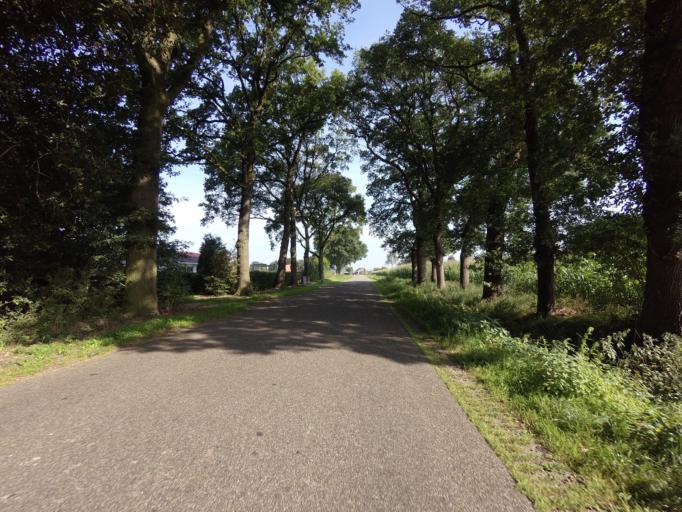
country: DE
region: Lower Saxony
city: Wielen
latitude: 52.5625
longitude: 6.6698
